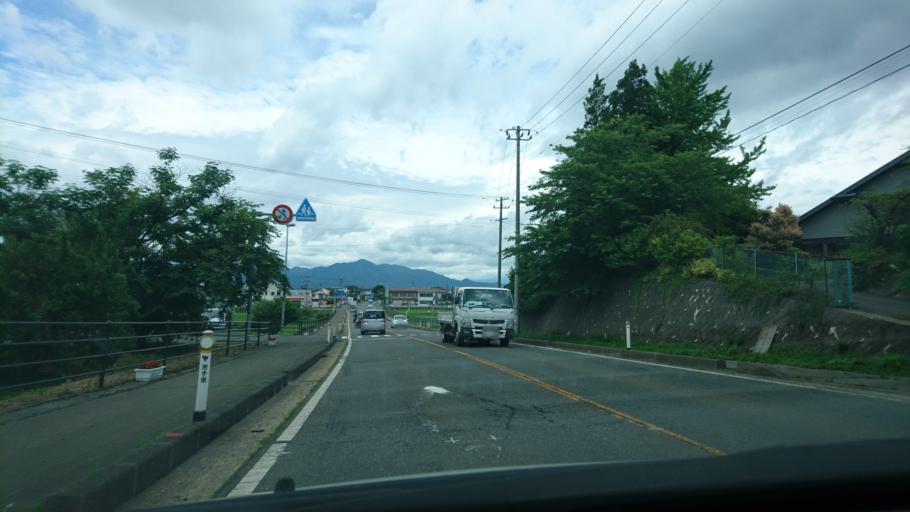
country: JP
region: Iwate
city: Morioka-shi
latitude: 39.6151
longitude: 141.1968
